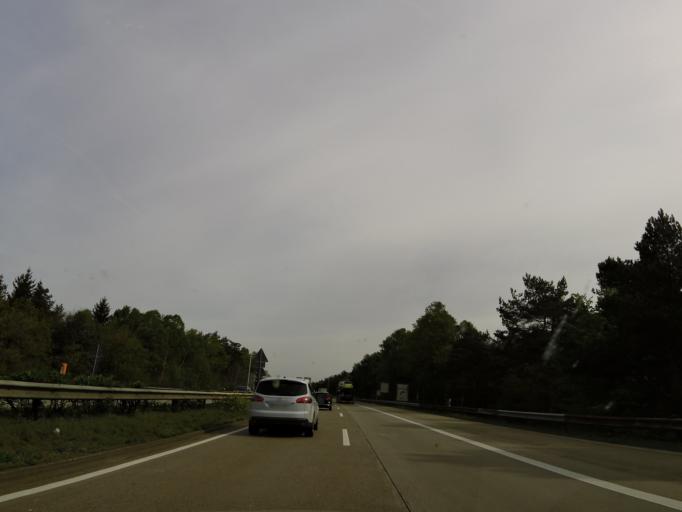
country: DE
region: Lower Saxony
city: Soltau
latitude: 52.9845
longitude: 9.9284
